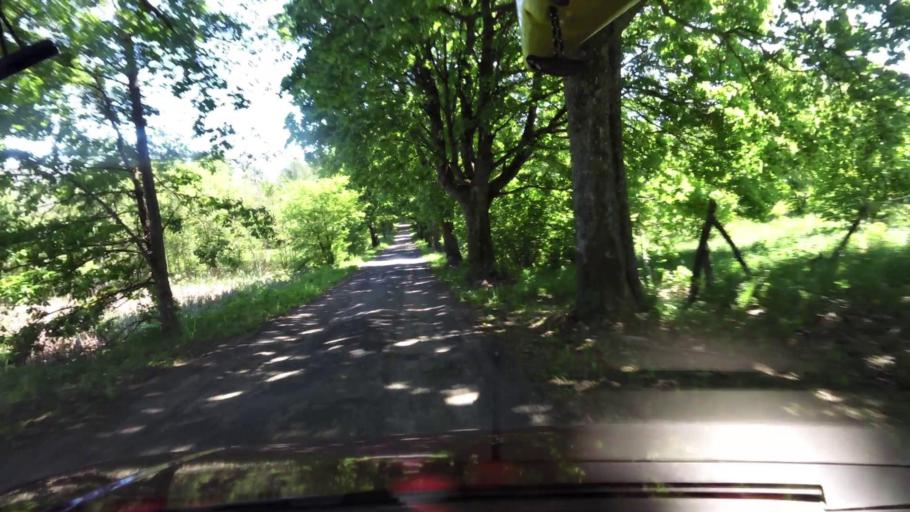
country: PL
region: West Pomeranian Voivodeship
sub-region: Powiat koszalinski
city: Polanow
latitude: 54.0373
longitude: 16.7756
